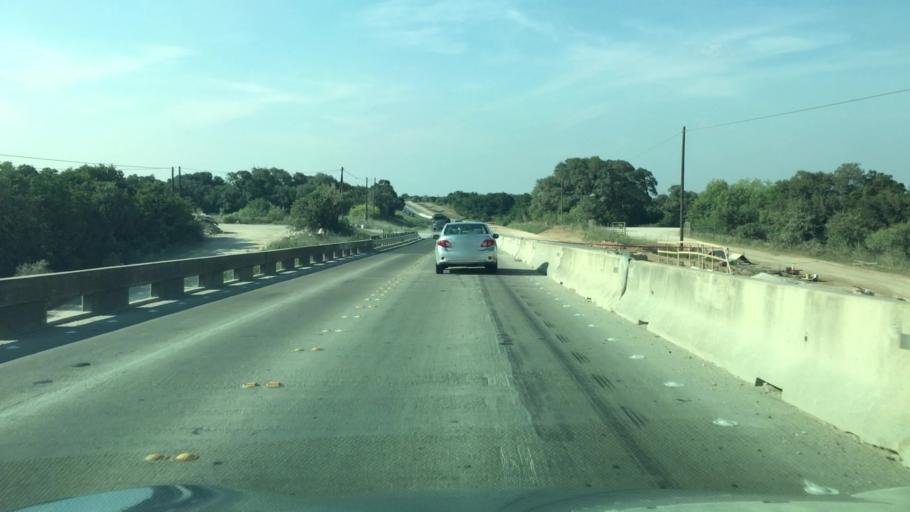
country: US
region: Texas
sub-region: Hays County
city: Buda
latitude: 30.0586
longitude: -97.8740
